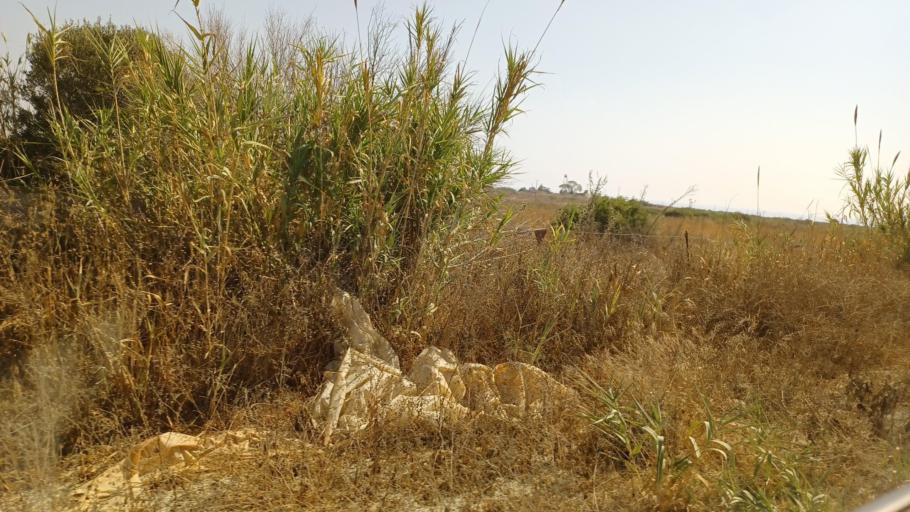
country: CY
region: Ammochostos
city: Deryneia
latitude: 35.0665
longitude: 33.9802
